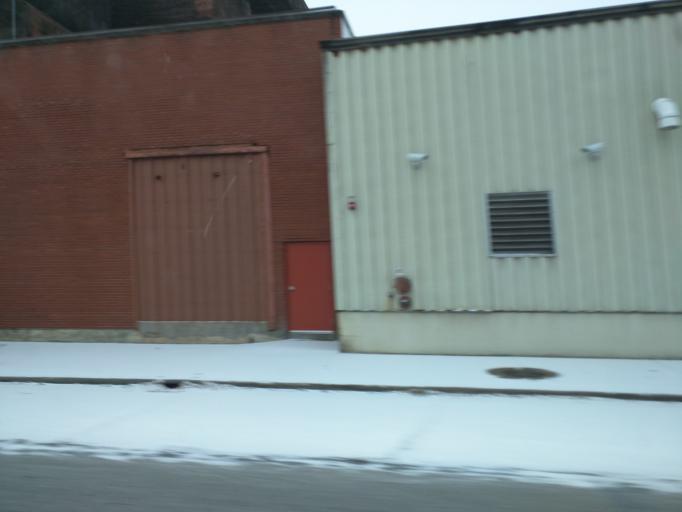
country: US
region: Wisconsin
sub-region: La Crosse County
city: La Crosse
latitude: 43.8038
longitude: -91.2535
